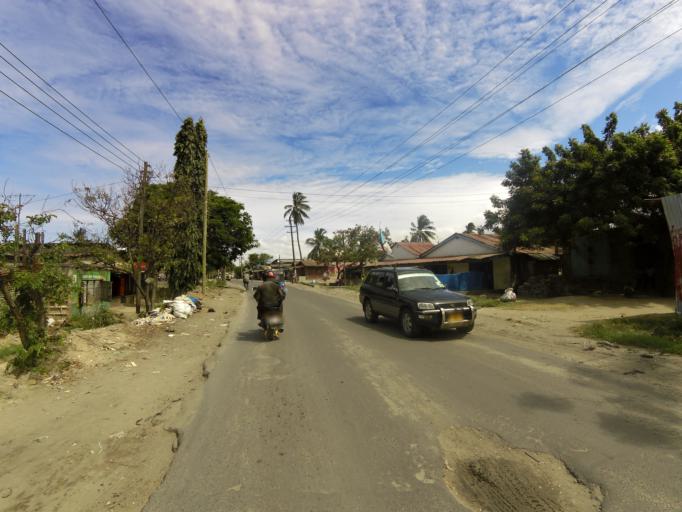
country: TZ
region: Dar es Salaam
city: Magomeni
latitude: -6.7949
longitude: 39.2468
